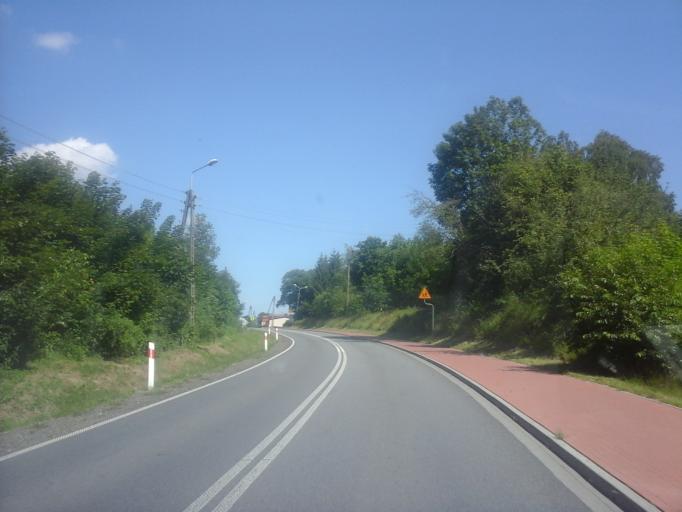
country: PL
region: West Pomeranian Voivodeship
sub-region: Koszalin
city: Koszalin
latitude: 54.0633
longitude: 16.1664
